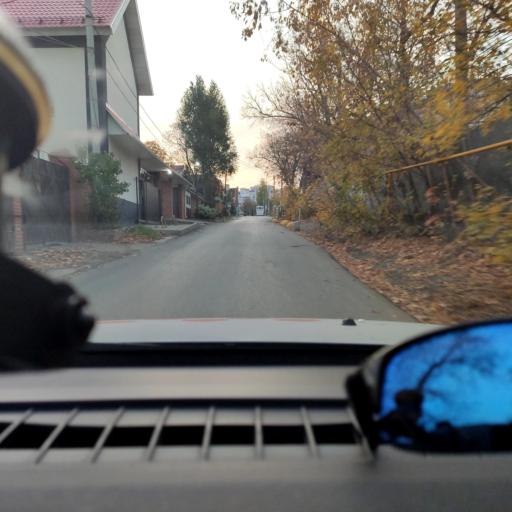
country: RU
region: Samara
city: Samara
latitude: 53.2327
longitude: 50.1770
